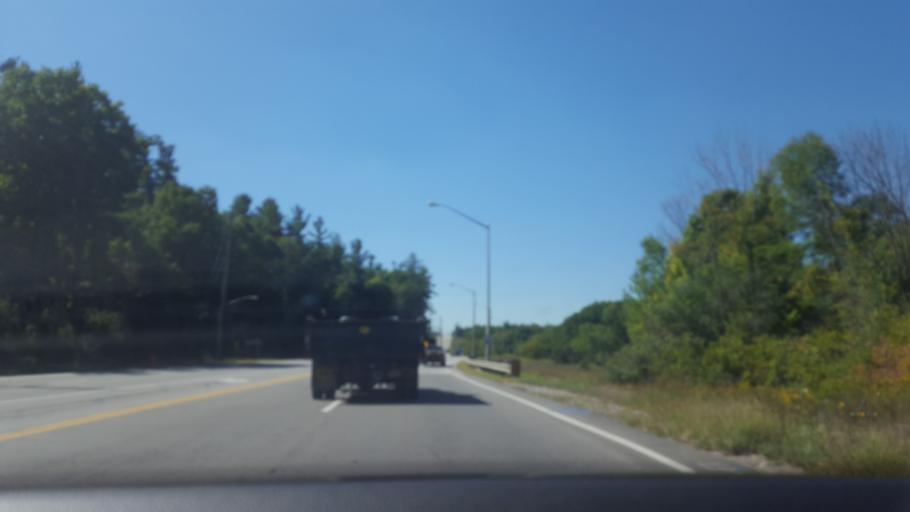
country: CA
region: Ontario
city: Vaughan
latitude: 43.8207
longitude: -79.5826
